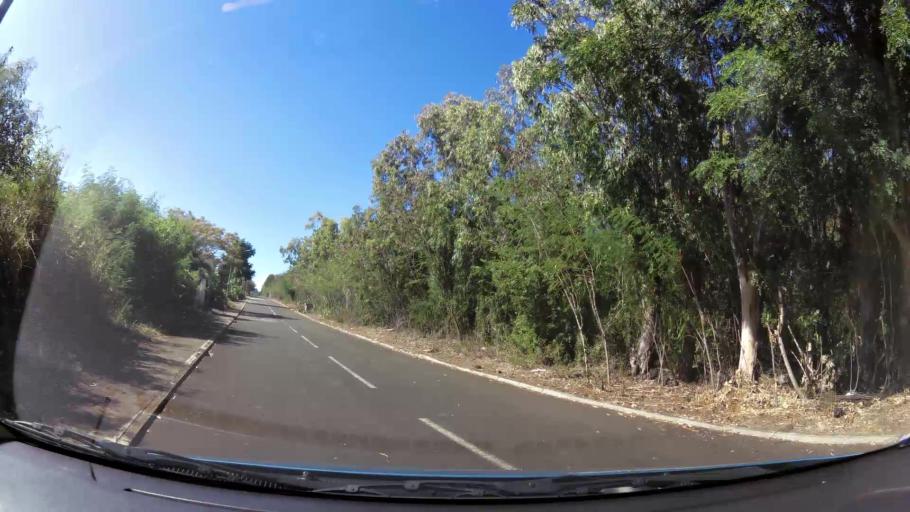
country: MU
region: Black River
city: Flic en Flac
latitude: -20.2862
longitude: 57.3743
